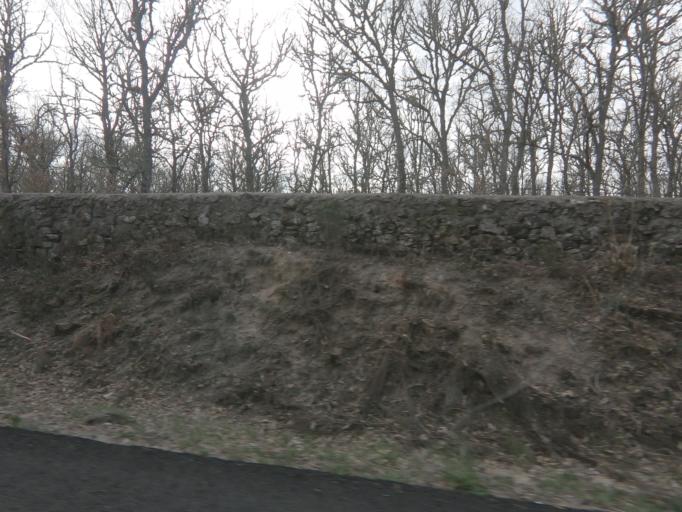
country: ES
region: Castille and Leon
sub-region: Provincia de Salamanca
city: Villasrubias
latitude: 40.3199
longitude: -6.6478
